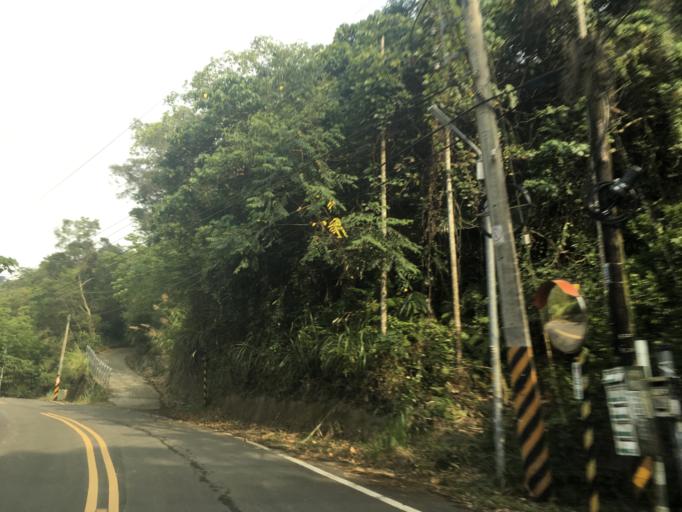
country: TW
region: Taiwan
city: Fengyuan
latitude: 24.2233
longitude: 120.7577
